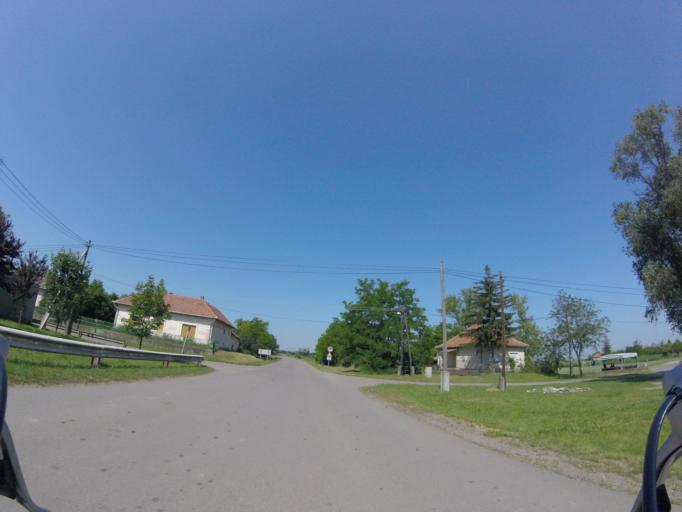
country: HU
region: Jasz-Nagykun-Szolnok
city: Tiszasuly
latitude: 47.4905
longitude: 20.3415
